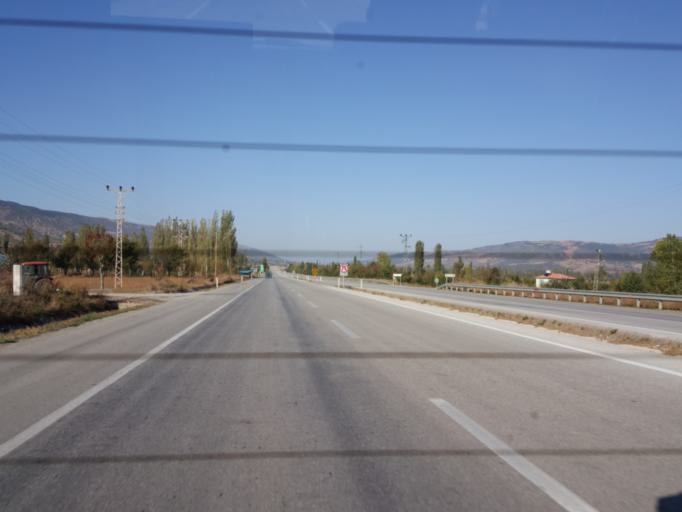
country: TR
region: Amasya
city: Ezinepazari
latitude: 40.5711
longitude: 36.1027
